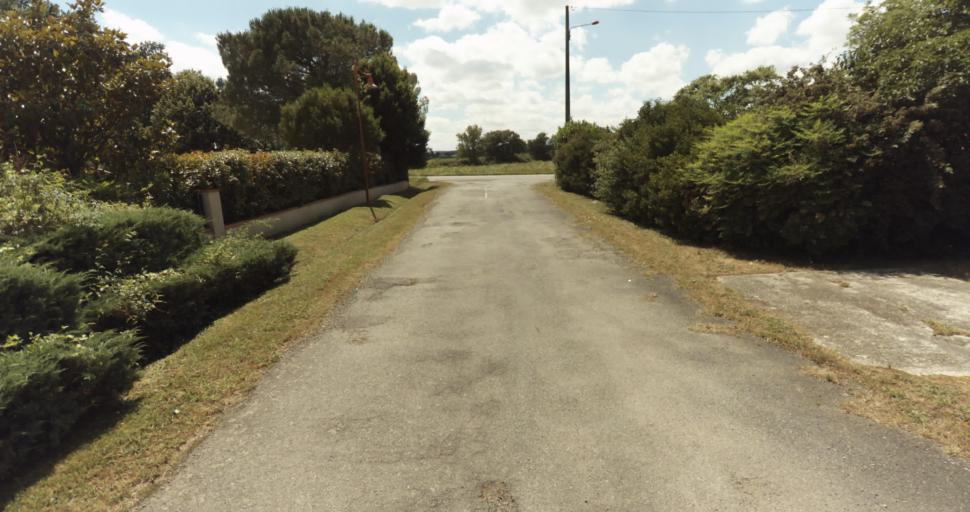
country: FR
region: Midi-Pyrenees
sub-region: Departement de la Haute-Garonne
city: Fontenilles
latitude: 43.5645
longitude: 1.1962
